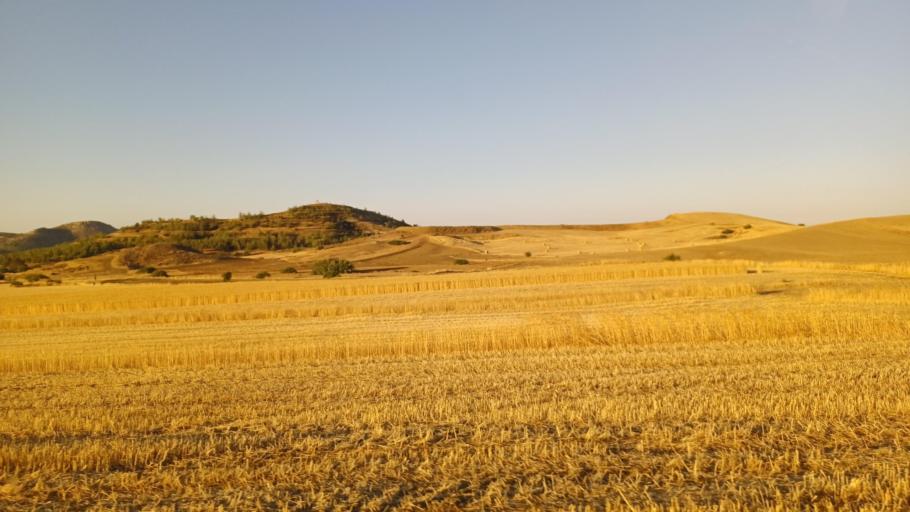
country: CY
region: Larnaka
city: Troulloi
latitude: 35.0257
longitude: 33.6345
